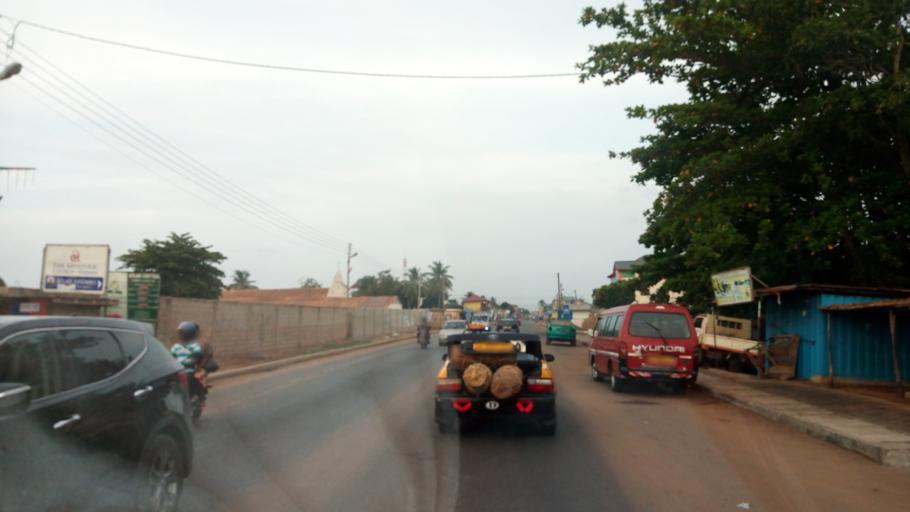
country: TG
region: Maritime
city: Lome
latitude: 6.1207
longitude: 1.1817
